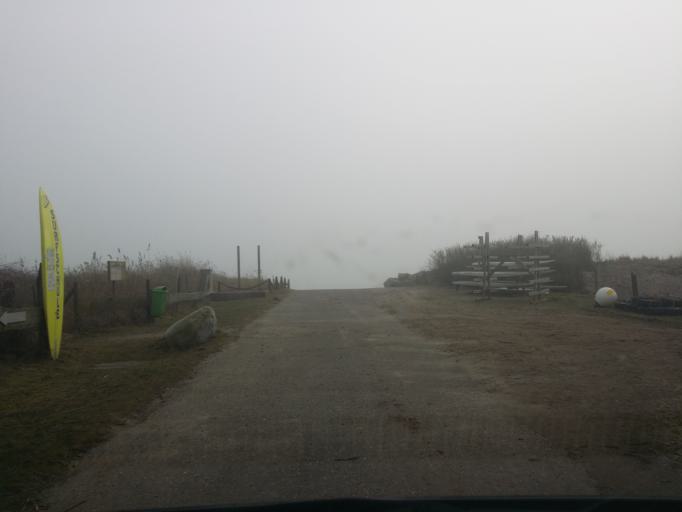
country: DE
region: Schleswig-Holstein
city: Burg auf Fehmarn
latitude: 54.4122
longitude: 11.2498
